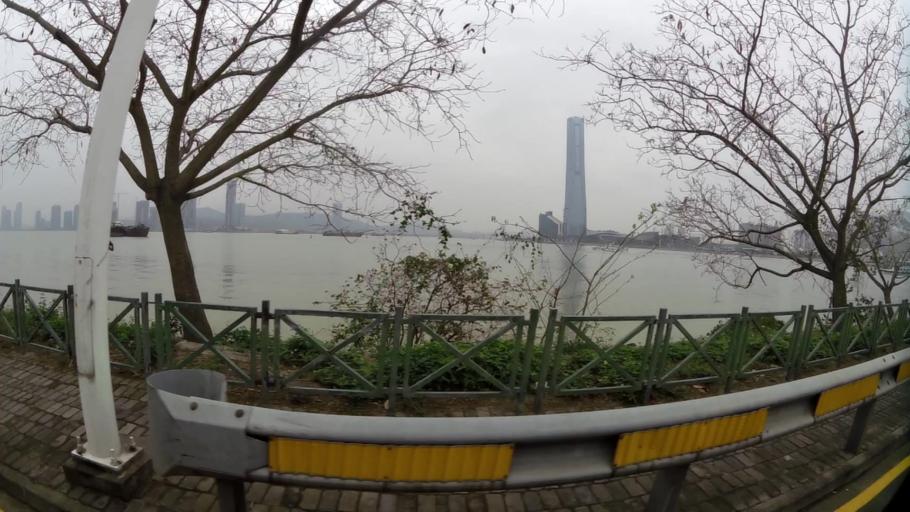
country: CN
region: Guangdong
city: Wanzai
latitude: 22.1804
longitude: 113.5309
